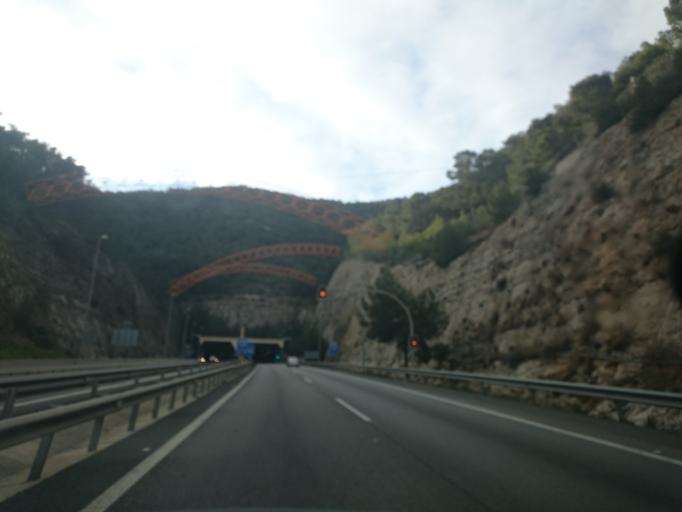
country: ES
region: Catalonia
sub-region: Provincia de Barcelona
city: Sitges
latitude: 41.2461
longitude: 1.8456
